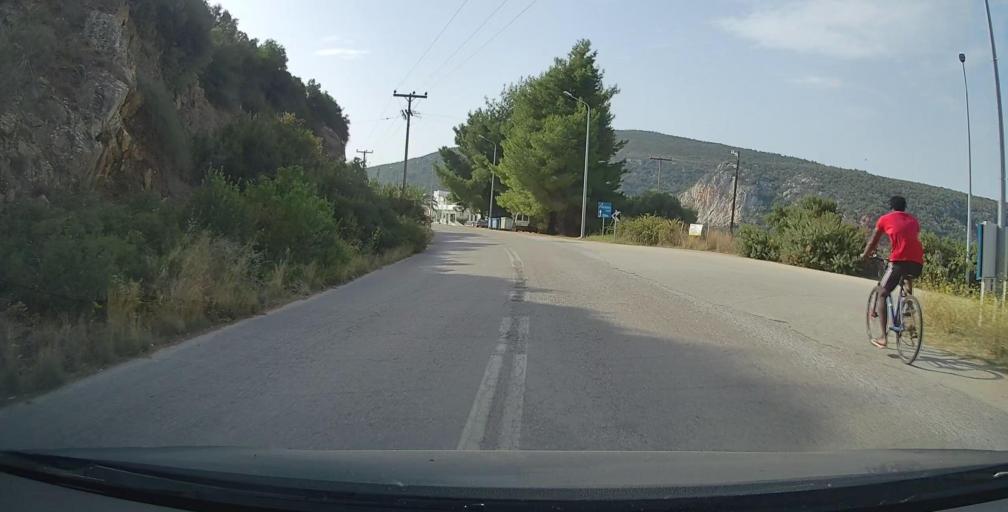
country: GR
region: Central Macedonia
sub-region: Nomos Chalkidikis
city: Sykia
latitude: 39.9646
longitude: 23.9265
